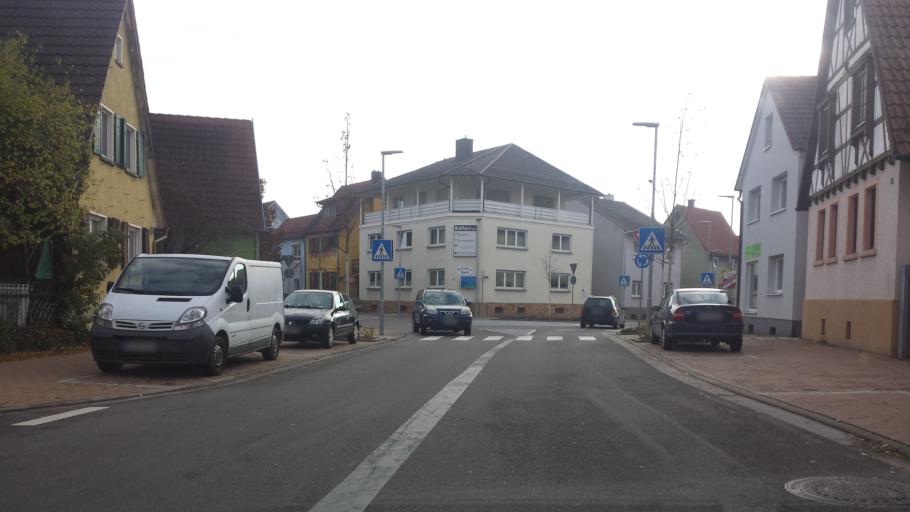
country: DE
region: Baden-Wuerttemberg
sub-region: Karlsruhe Region
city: Sankt Leon-Rot
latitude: 49.2628
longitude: 8.6326
